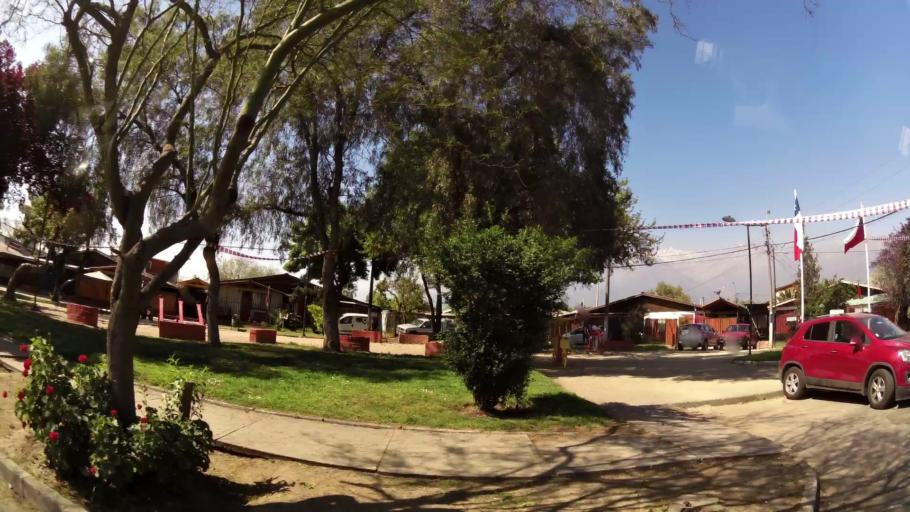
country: CL
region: Santiago Metropolitan
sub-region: Provincia de Santiago
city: Villa Presidente Frei, Nunoa, Santiago, Chile
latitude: -33.4985
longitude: -70.5796
